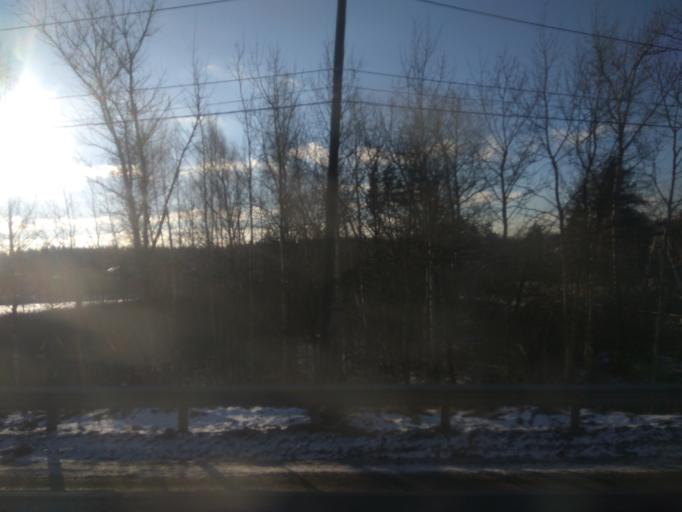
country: RU
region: Moskovskaya
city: Gzhel'
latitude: 55.6308
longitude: 38.3598
